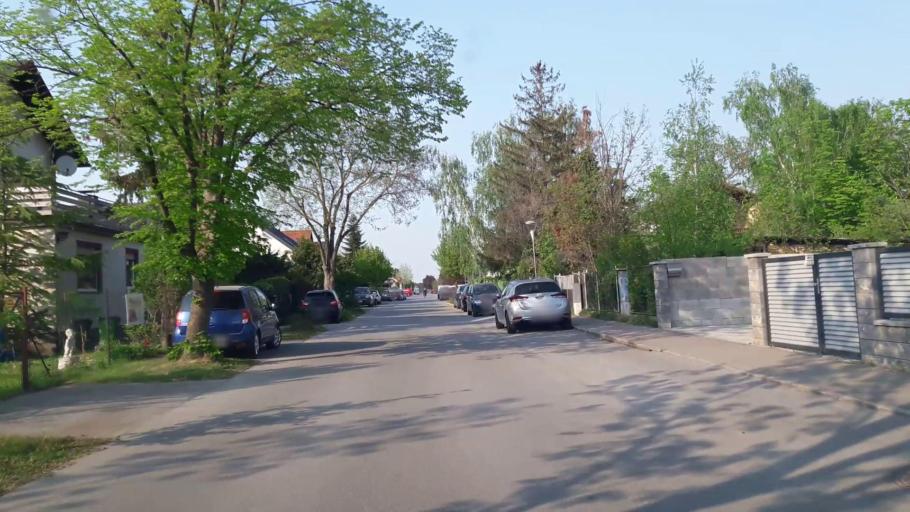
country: AT
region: Lower Austria
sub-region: Politischer Bezirk Ganserndorf
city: Deutsch-Wagram
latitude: 48.3168
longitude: 16.5810
